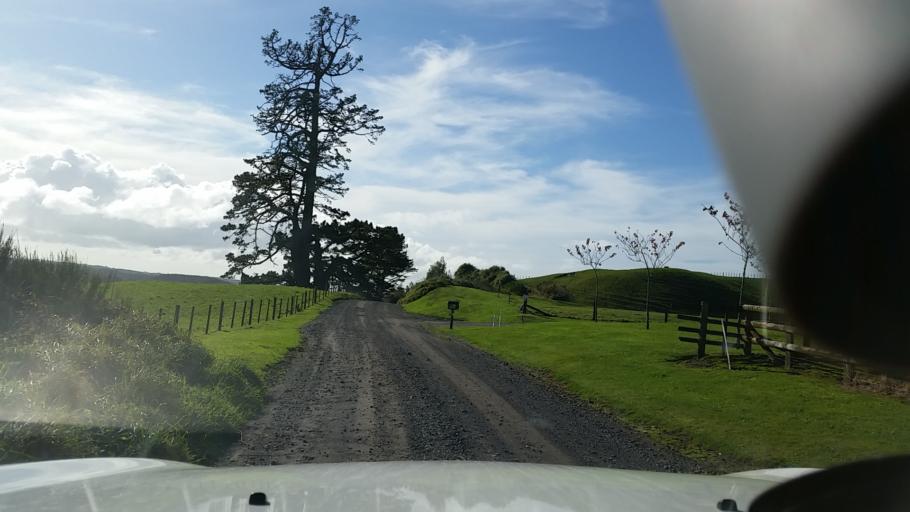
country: NZ
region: Bay of Plenty
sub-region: Rotorua District
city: Rotorua
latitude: -38.0245
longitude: 176.2837
